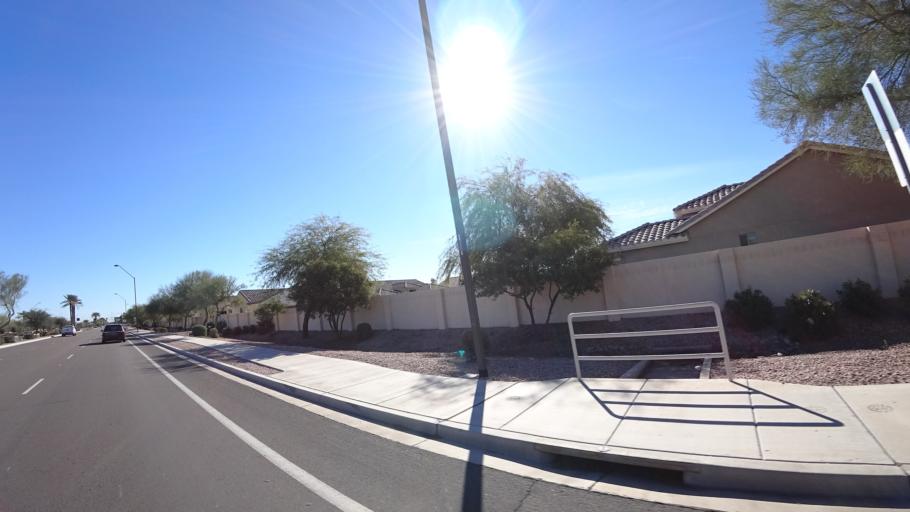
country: US
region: Arizona
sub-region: Maricopa County
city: Litchfield Park
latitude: 33.4936
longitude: -112.4042
